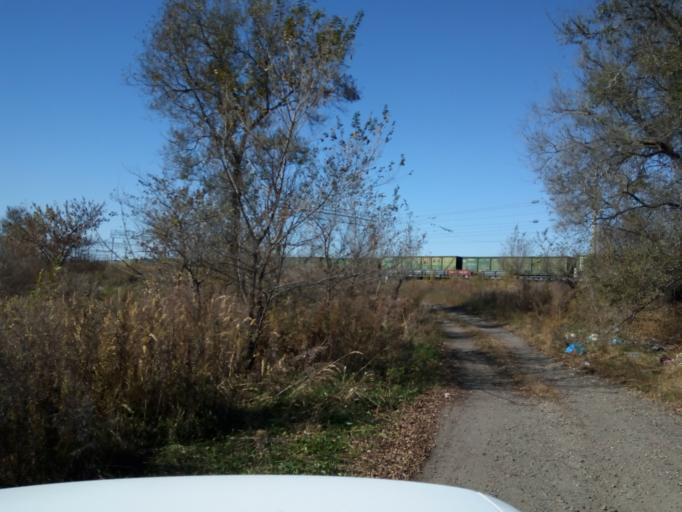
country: RU
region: Primorskiy
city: Dal'nerechensk
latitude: 45.9107
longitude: 133.7929
